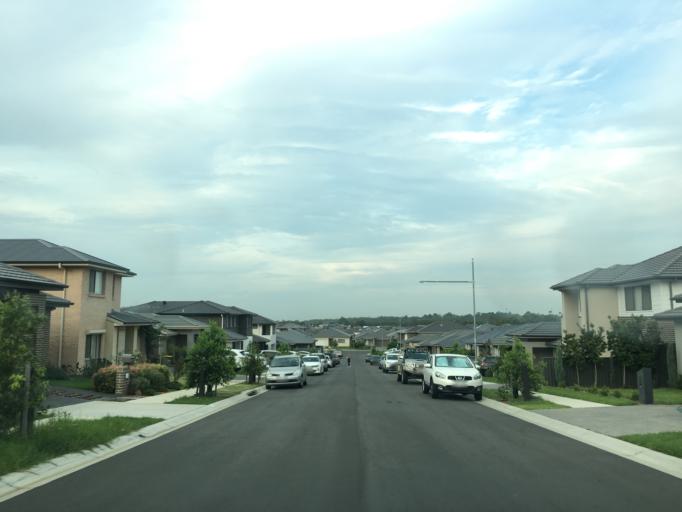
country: AU
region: New South Wales
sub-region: Campbelltown Municipality
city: Denham Court
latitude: -33.9820
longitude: 150.8058
